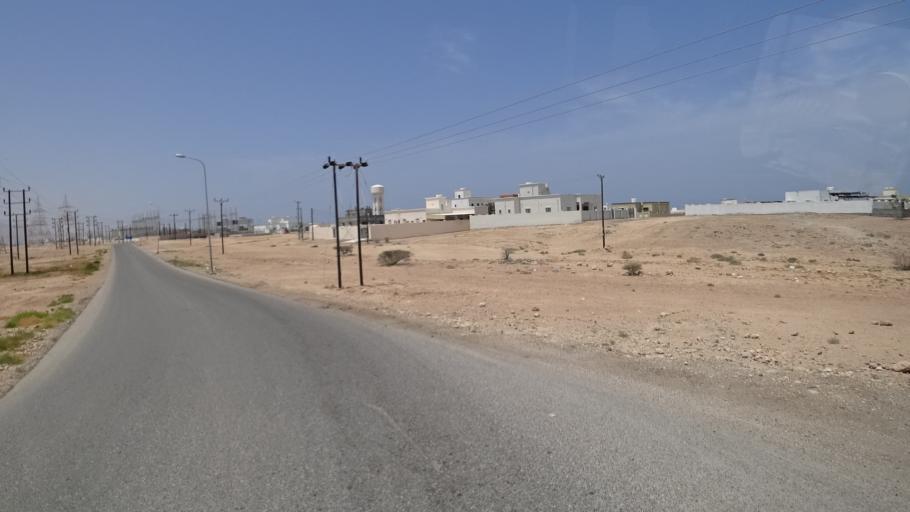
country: OM
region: Ash Sharqiyah
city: Sur
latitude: 22.6156
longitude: 59.4555
